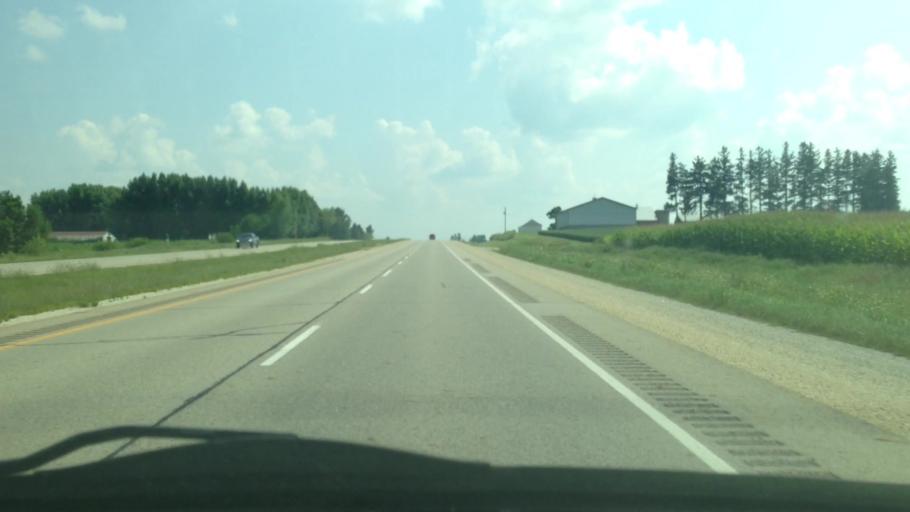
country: US
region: Iowa
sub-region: Bremer County
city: Denver
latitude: 42.6372
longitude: -92.3377
